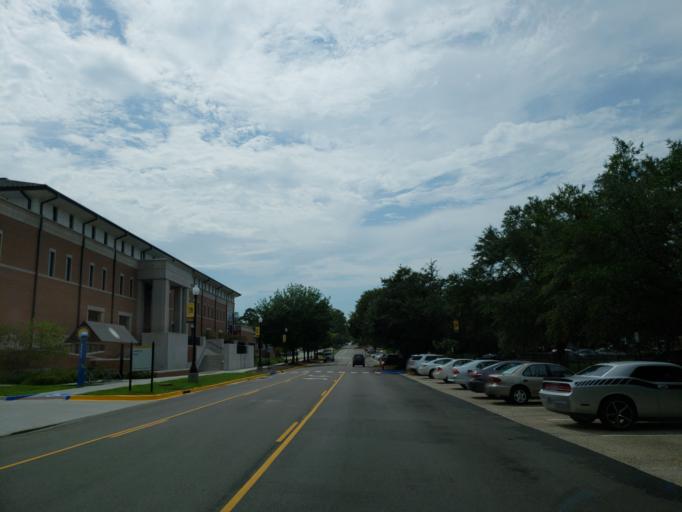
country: US
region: Mississippi
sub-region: Lamar County
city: Arnold Line
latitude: 31.3284
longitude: -89.3375
